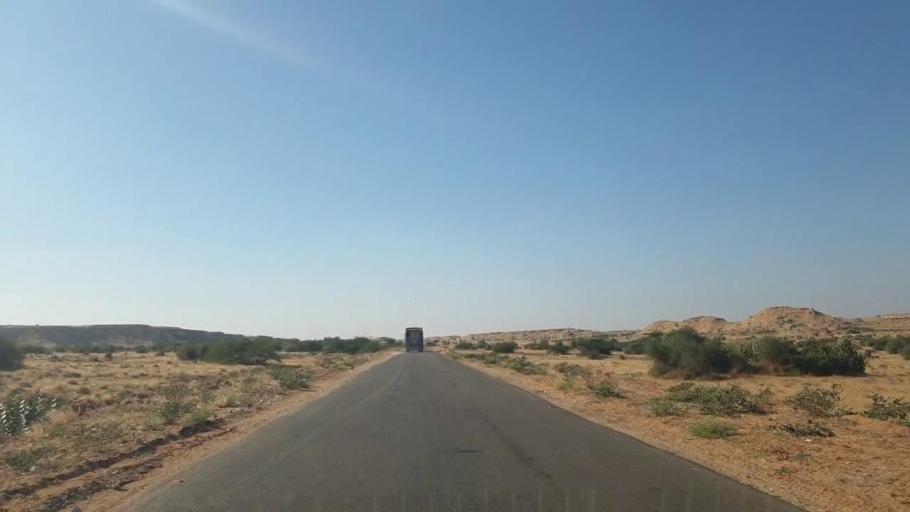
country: PK
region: Sindh
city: Gharo
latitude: 25.2208
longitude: 67.6192
